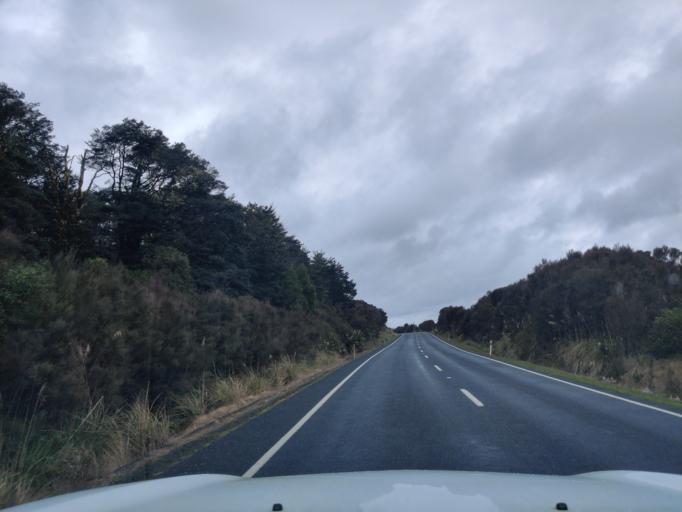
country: NZ
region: Manawatu-Wanganui
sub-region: Ruapehu District
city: Waiouru
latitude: -39.3346
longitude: 175.3802
